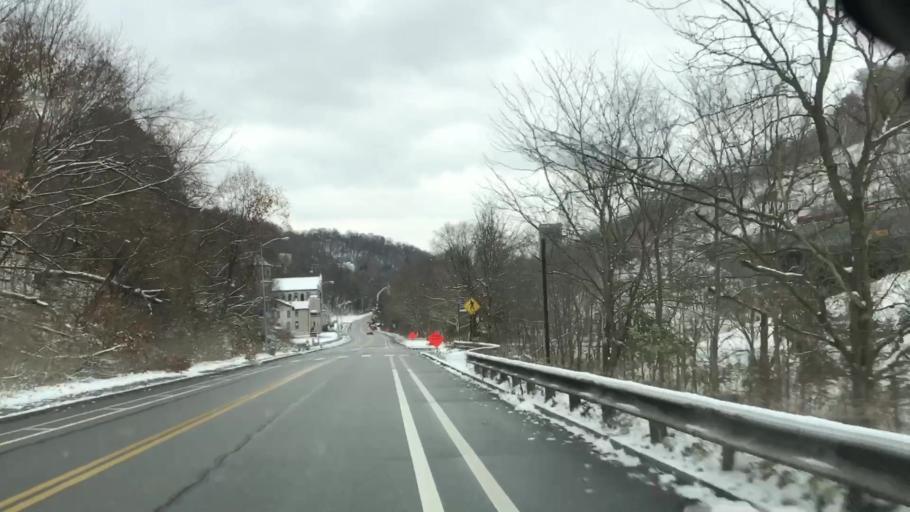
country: US
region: Pennsylvania
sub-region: Allegheny County
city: Millvale
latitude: 40.4695
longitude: -80.0018
